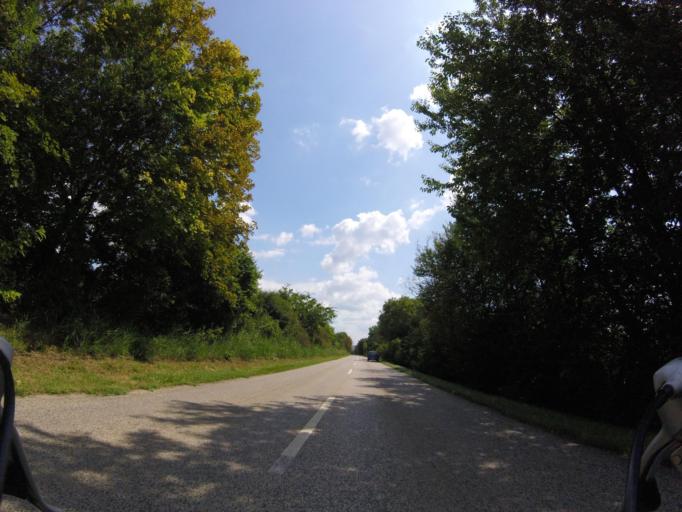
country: HU
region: Fejer
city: Etyek
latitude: 47.4835
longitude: 18.7725
